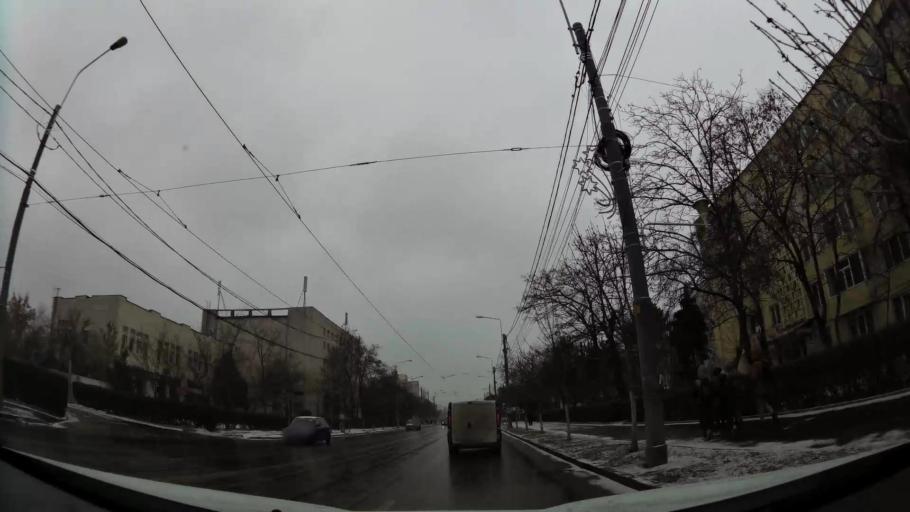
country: RO
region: Prahova
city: Ploiesti
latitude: 44.9546
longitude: 26.0028
